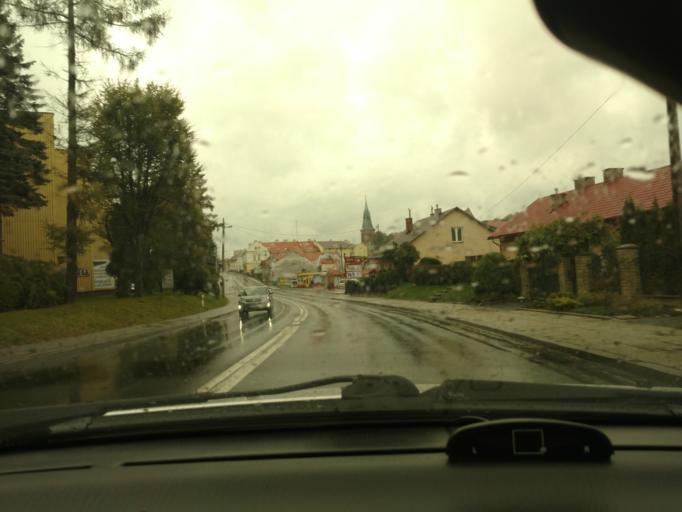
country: PL
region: Subcarpathian Voivodeship
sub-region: Powiat strzyzowski
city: Strzyzow
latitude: 49.8694
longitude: 21.7817
